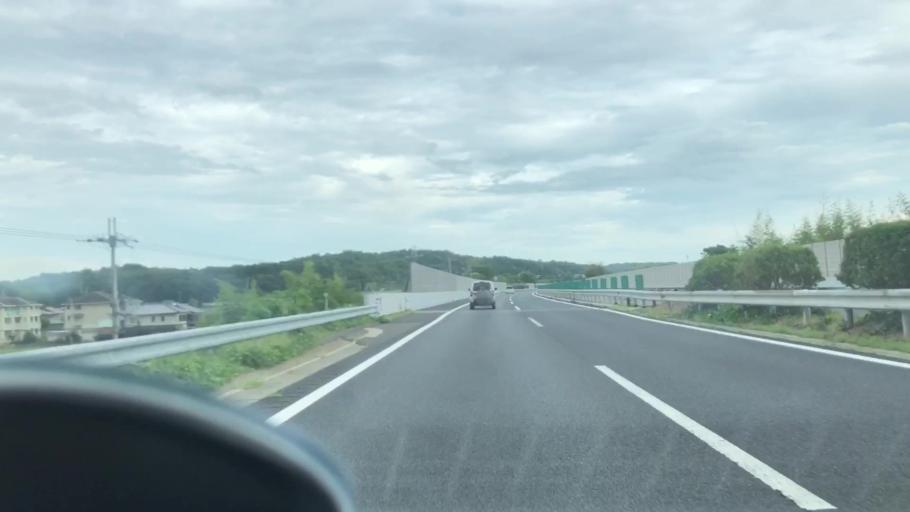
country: JP
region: Hyogo
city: Yashiro
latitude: 34.9281
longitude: 134.9831
